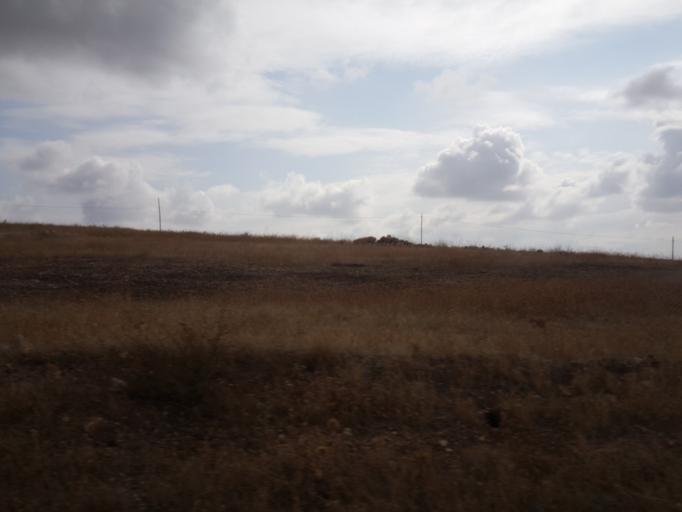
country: TR
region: Kirikkale
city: Keskin
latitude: 39.6400
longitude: 33.6084
